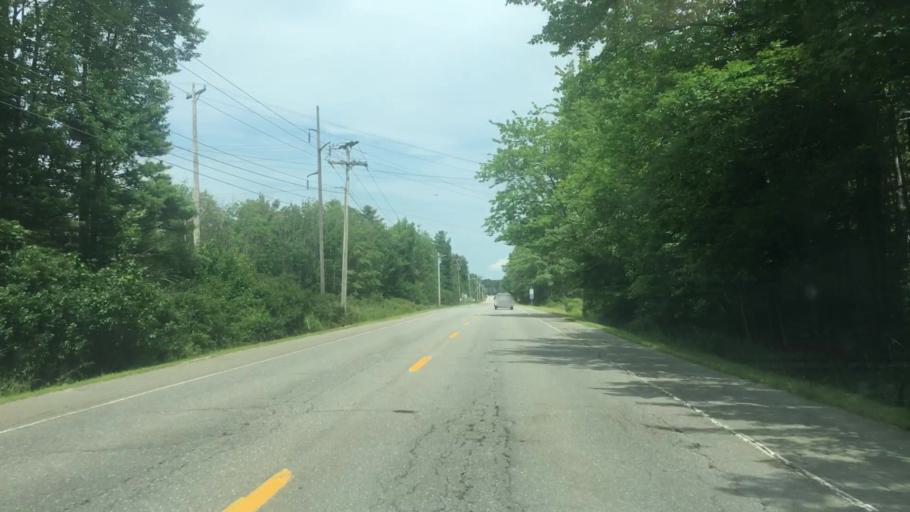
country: US
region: Maine
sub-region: Cumberland County
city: Scarborough
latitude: 43.5987
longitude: -70.2896
